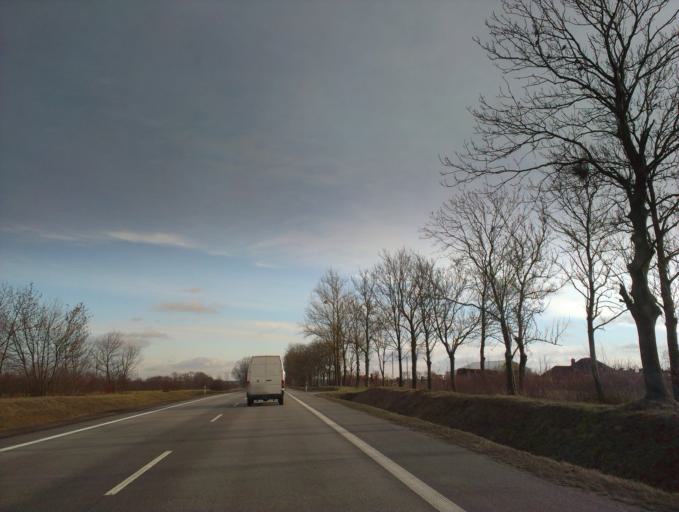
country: PL
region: Kujawsko-Pomorskie
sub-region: Powiat lipnowski
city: Kikol
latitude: 52.9304
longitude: 19.0719
